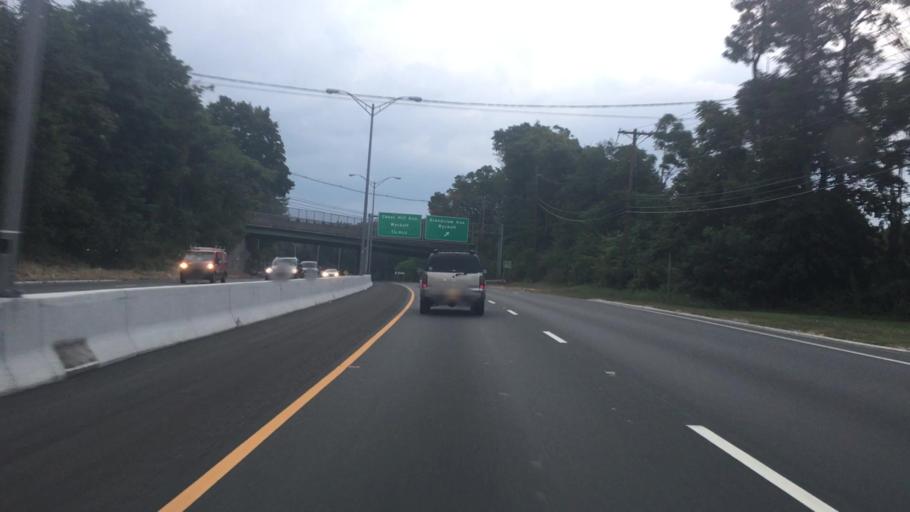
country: US
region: New Jersey
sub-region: Bergen County
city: Midland Park
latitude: 40.9778
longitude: -74.1600
